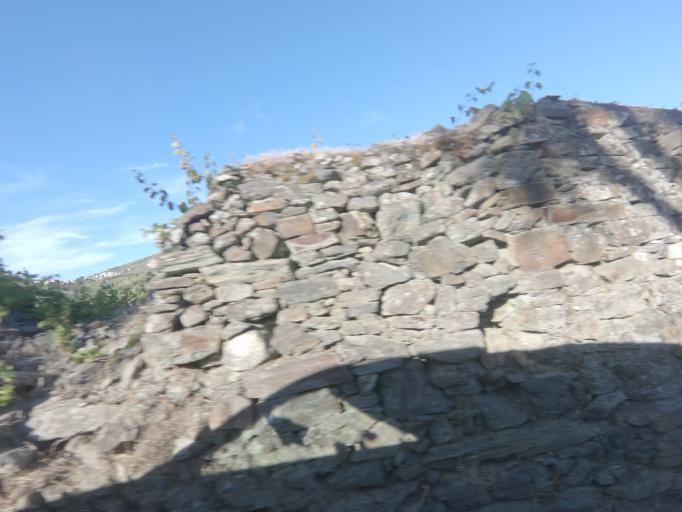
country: PT
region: Vila Real
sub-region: Peso da Regua
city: Peso da Regua
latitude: 41.1729
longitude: -7.7817
